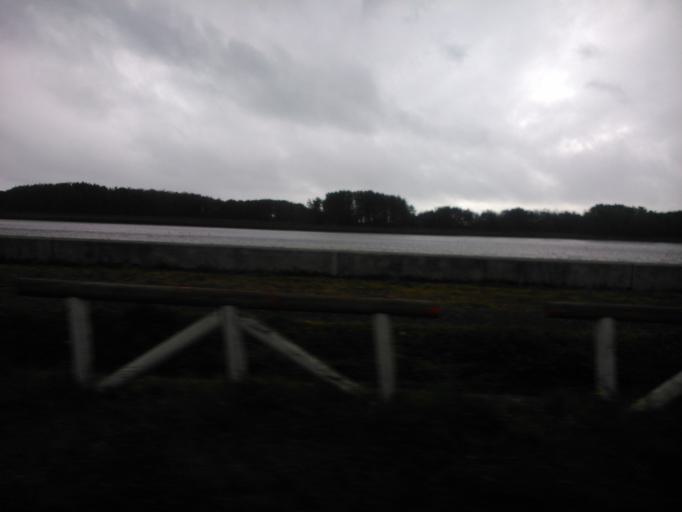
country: CL
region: Araucania
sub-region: Provincia de Cautin
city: Carahue
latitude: -38.8021
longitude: -73.4004
